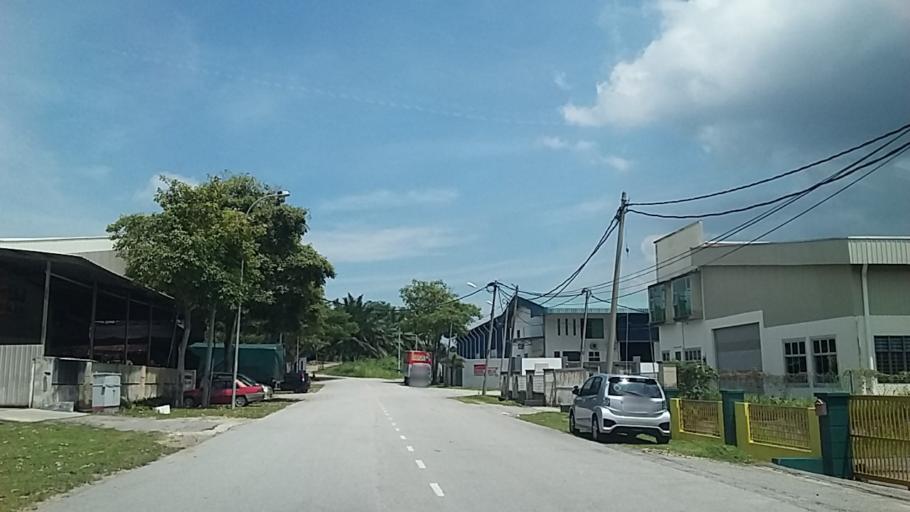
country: MY
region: Johor
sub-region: Daerah Batu Pahat
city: Batu Pahat
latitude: 1.7827
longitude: 102.9665
